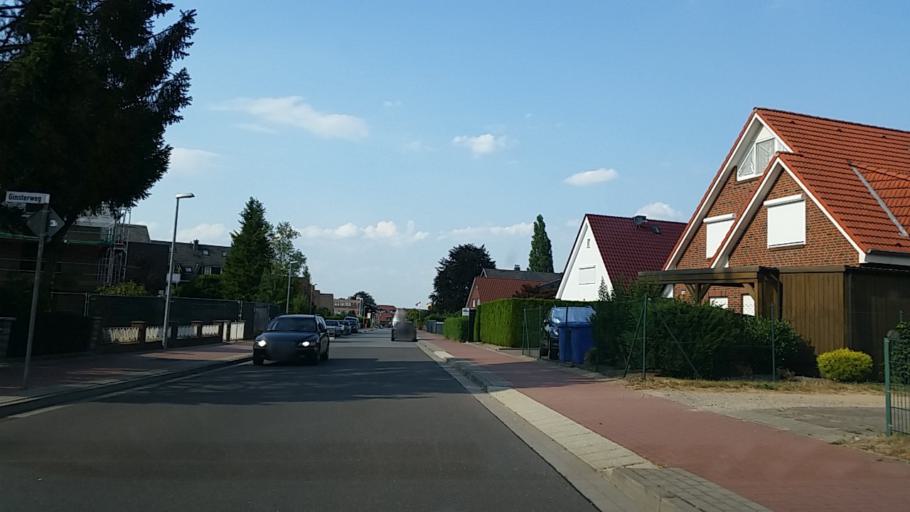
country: DE
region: Lower Saxony
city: Neu Wulmstorf
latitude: 53.4613
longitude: 9.8005
